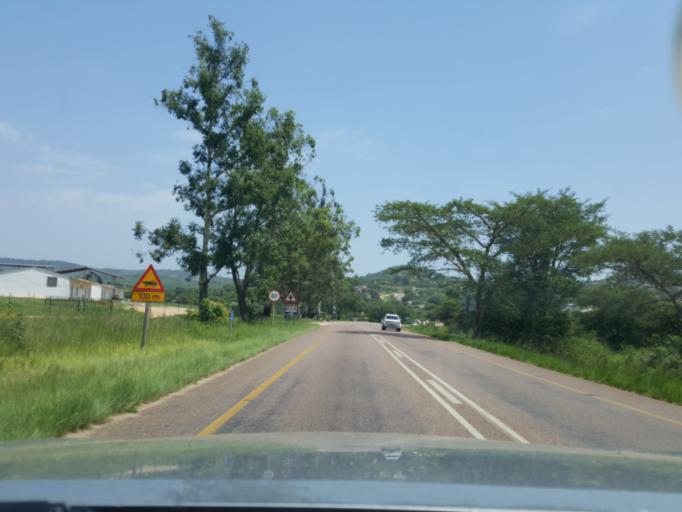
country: ZA
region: Mpumalanga
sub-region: Ehlanzeni District
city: Graksop
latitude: -24.9895
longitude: 31.1110
